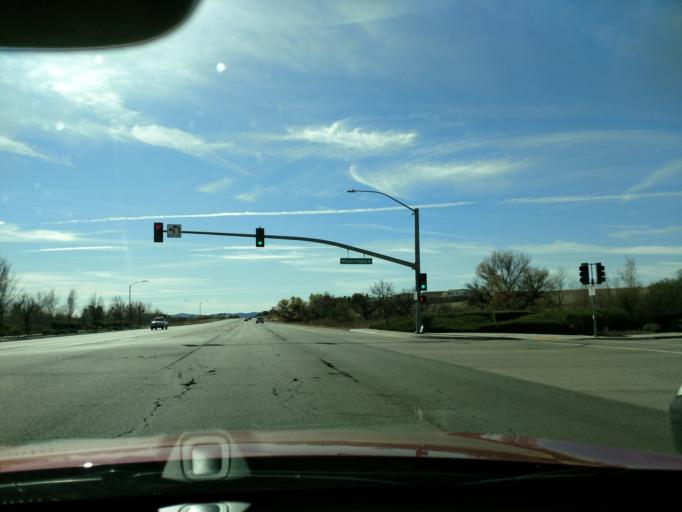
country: US
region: California
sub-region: Riverside County
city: Murrieta Hot Springs
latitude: 33.6154
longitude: -117.1037
